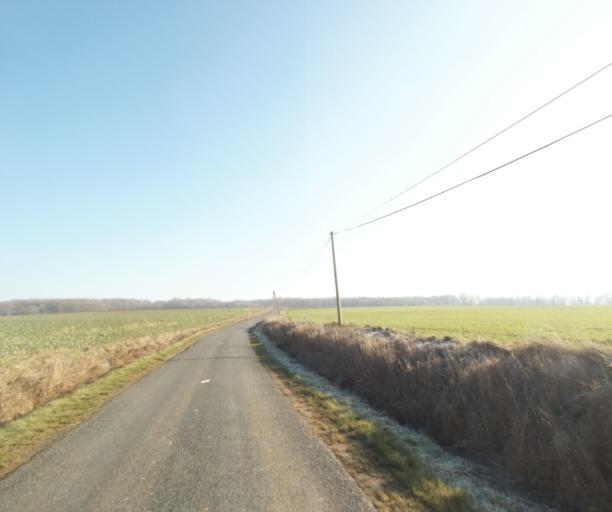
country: FR
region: Champagne-Ardenne
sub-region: Departement de la Haute-Marne
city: Bienville
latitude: 48.5096
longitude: 5.0188
